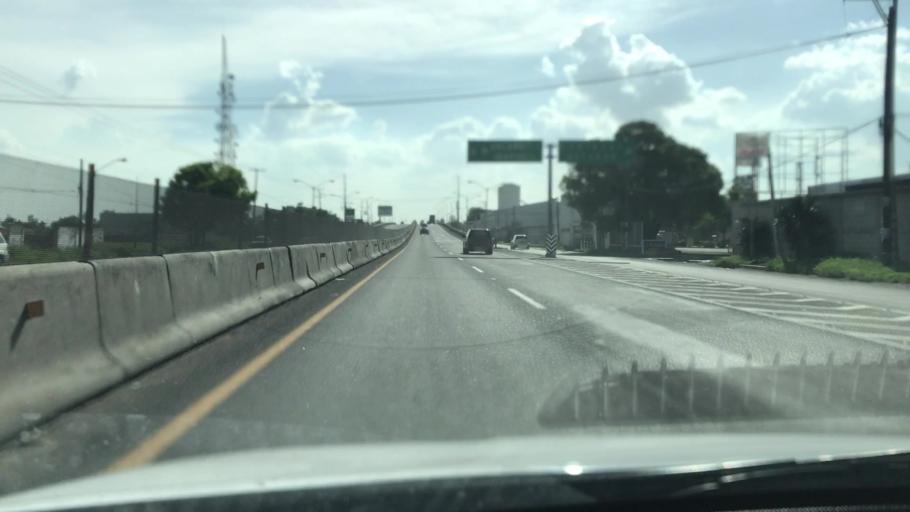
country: MX
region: Guanajuato
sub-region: Cortazar
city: Colonia la Calzada (La Olla)
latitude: 20.5115
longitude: -100.9502
